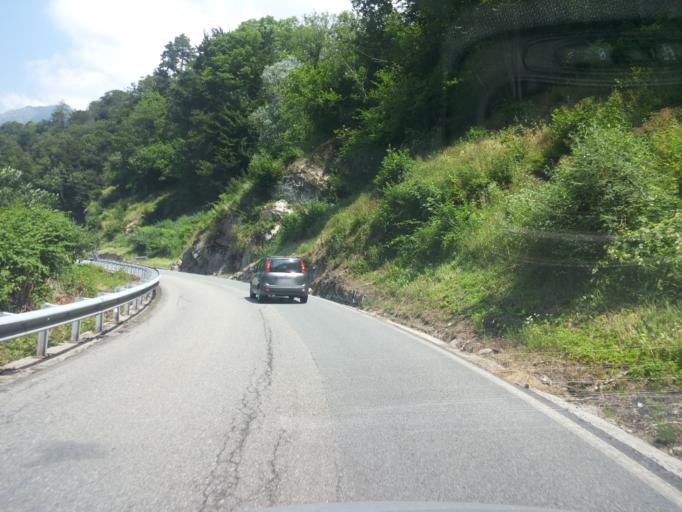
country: IT
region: Piedmont
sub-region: Provincia di Biella
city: San Paolo Cervo
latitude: 45.6527
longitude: 8.0129
